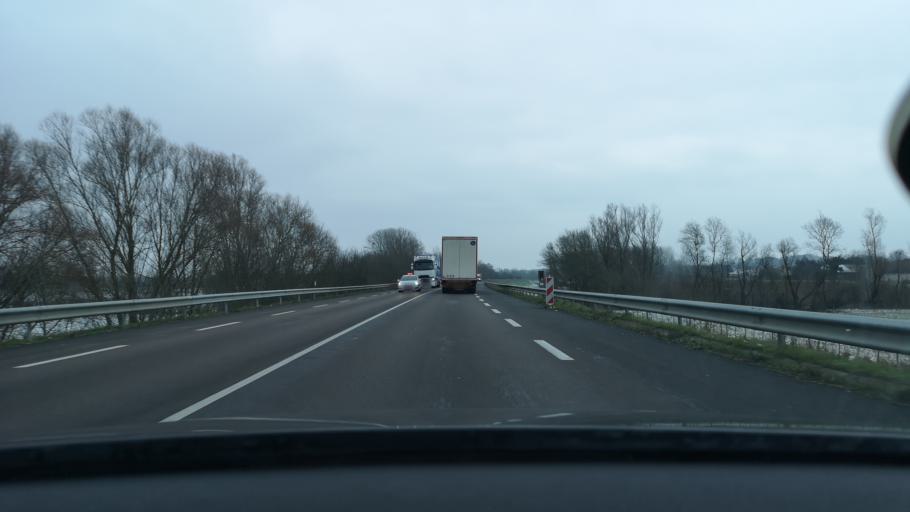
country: FR
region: Bourgogne
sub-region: Departement de Saone-et-Loire
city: Saint-Marcel
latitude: 46.7846
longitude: 4.8897
